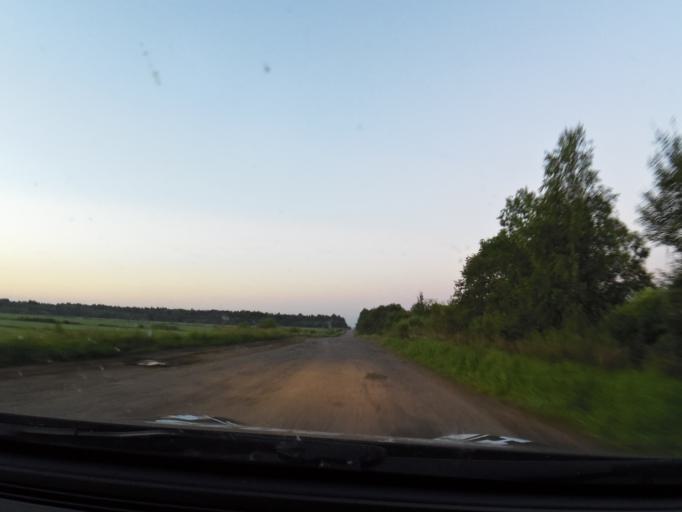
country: RU
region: Kostroma
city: Buy
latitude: 58.4811
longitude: 41.4598
